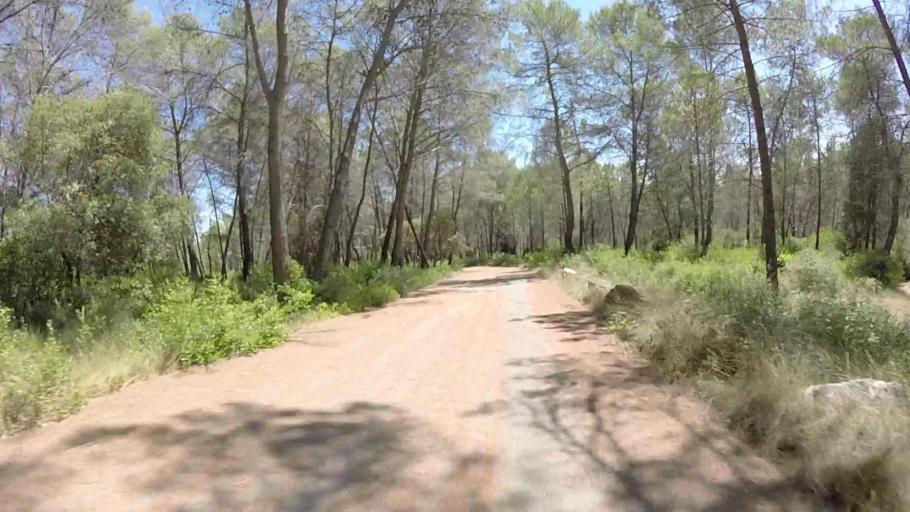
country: FR
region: Provence-Alpes-Cote d'Azur
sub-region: Departement des Alpes-Maritimes
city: Vallauris
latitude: 43.6089
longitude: 7.0462
